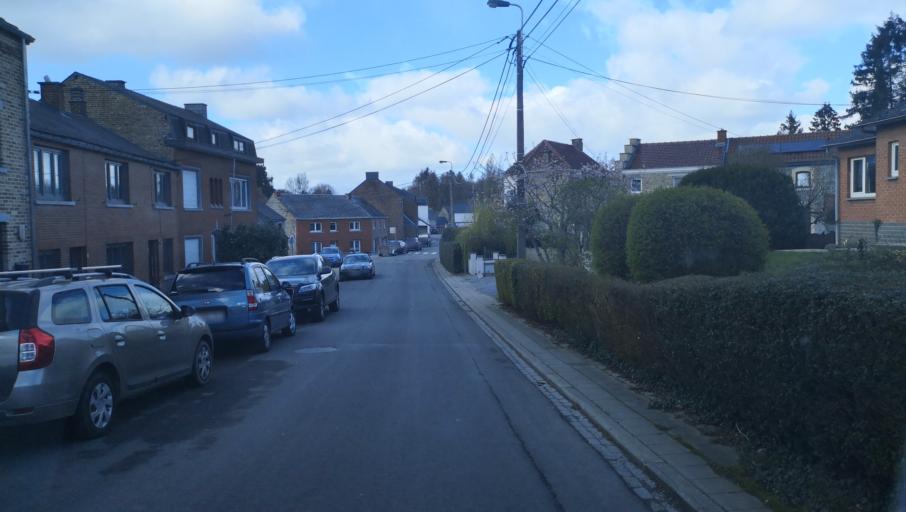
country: BE
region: Wallonia
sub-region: Province de Namur
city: Namur
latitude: 50.5012
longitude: 4.8724
